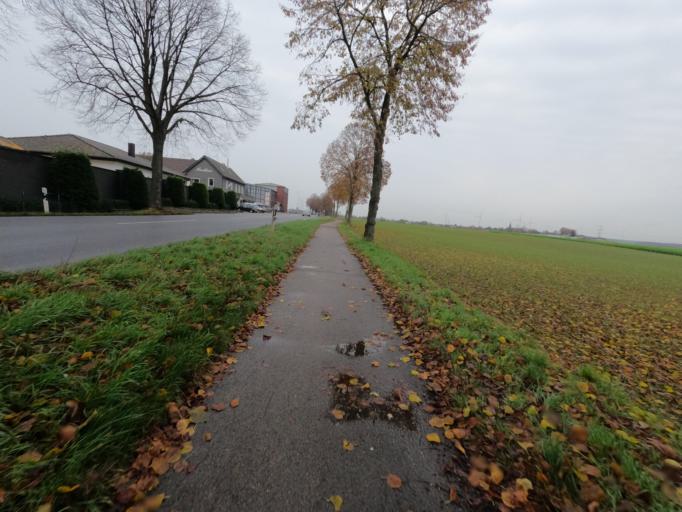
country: DE
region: North Rhine-Westphalia
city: Geilenkirchen
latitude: 50.9879
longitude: 6.1195
